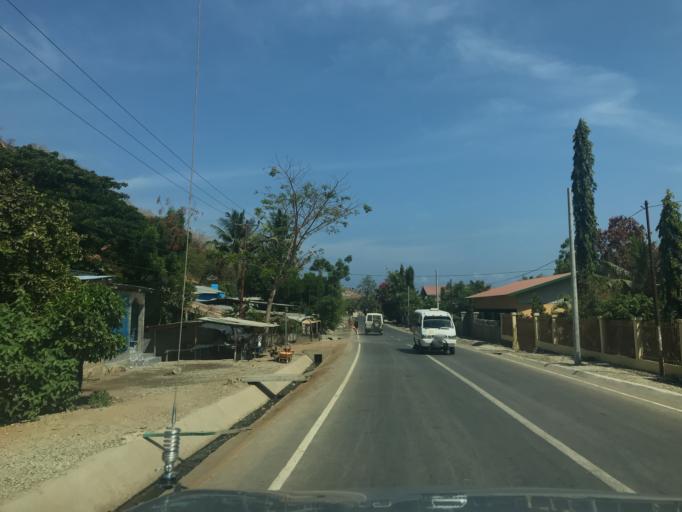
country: TL
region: Dili
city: Dili
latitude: -8.5583
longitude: 125.5205
